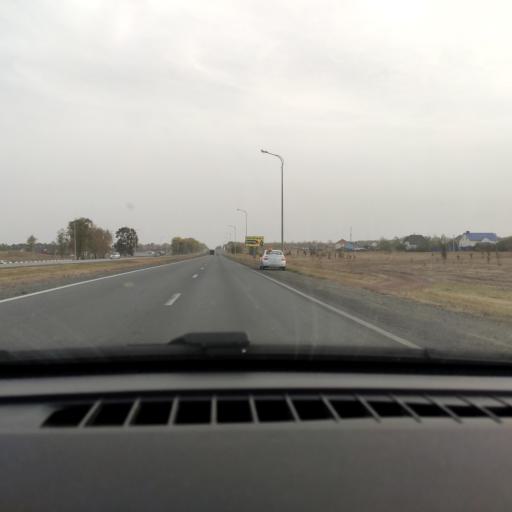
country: RU
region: Belgorod
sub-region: Belgorodskiy Rayon
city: Belgorod
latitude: 50.6546
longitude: 36.6920
